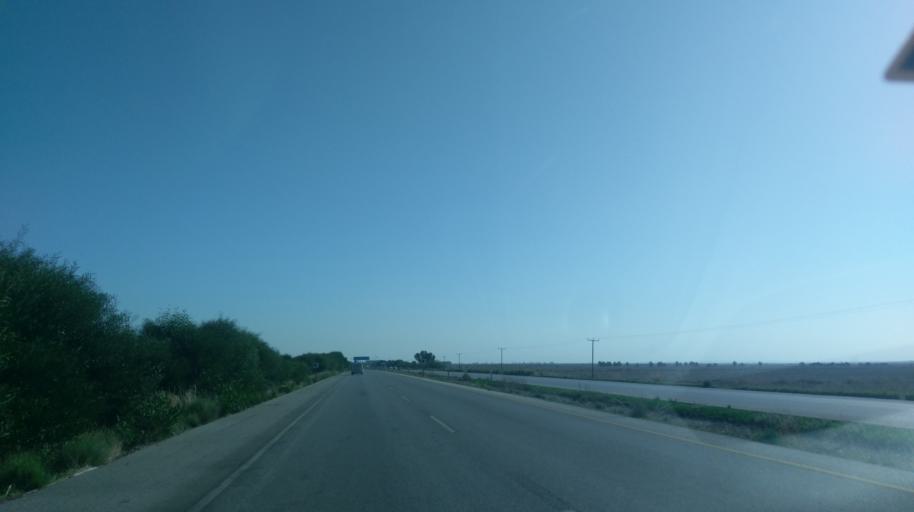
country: CY
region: Ammochostos
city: Lefkonoiko
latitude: 35.1835
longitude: 33.6926
